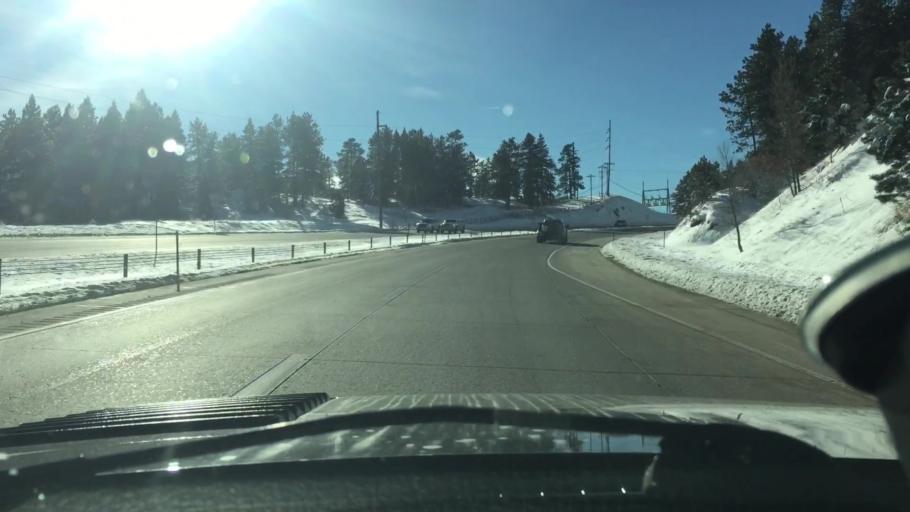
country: US
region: Colorado
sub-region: Jefferson County
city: Indian Hills
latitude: 39.5901
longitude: -105.2212
